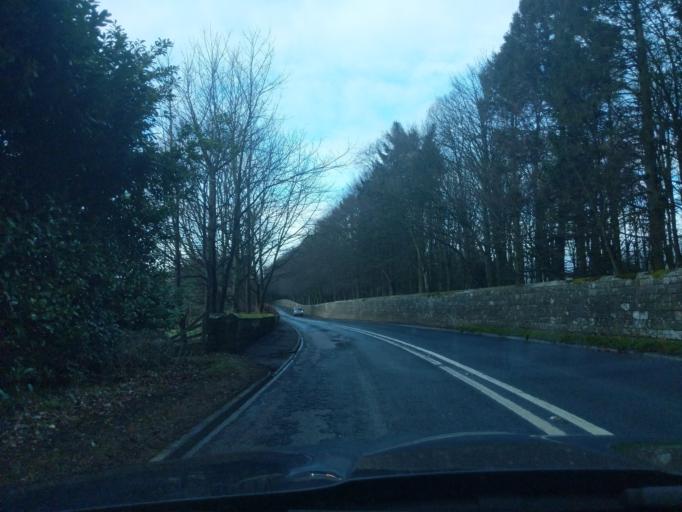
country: GB
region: England
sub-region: Northumberland
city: Alnwick
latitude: 55.4162
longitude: -1.6923
